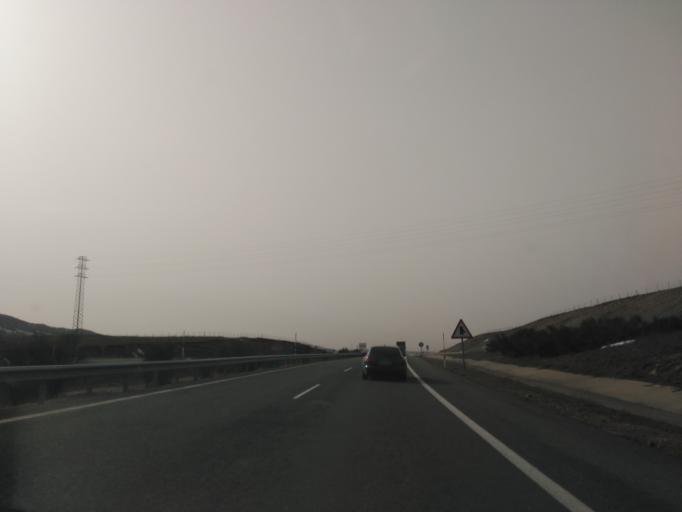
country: ES
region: Cantabria
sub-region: Provincia de Cantabria
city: Mataporquera
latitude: 42.8659
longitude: -4.1537
